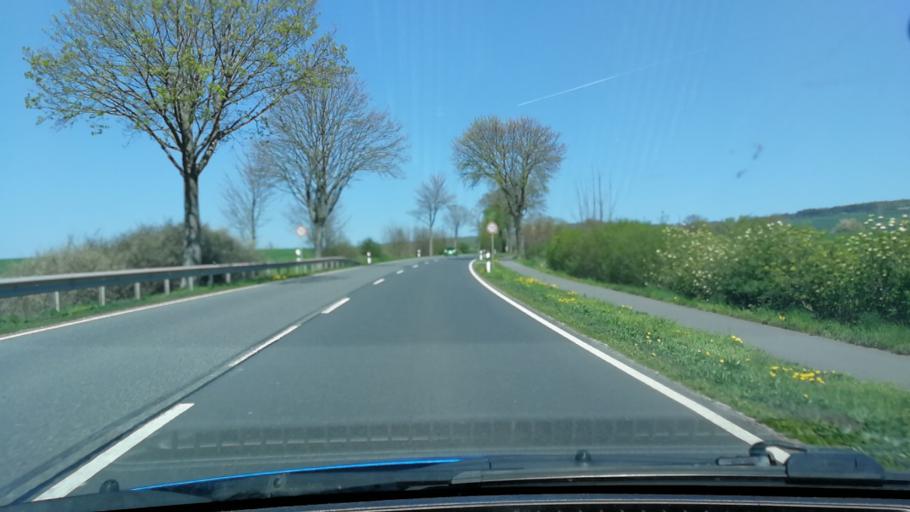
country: DE
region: Lower Saxony
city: Freden
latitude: 51.8760
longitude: 9.8790
